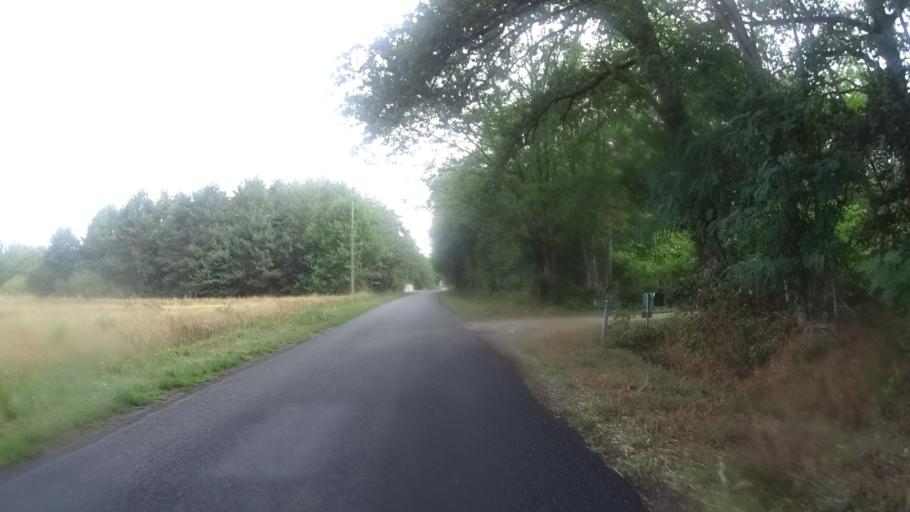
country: FR
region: Centre
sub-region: Departement du Loiret
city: Fay-aux-Loges
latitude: 47.9691
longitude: 2.1859
